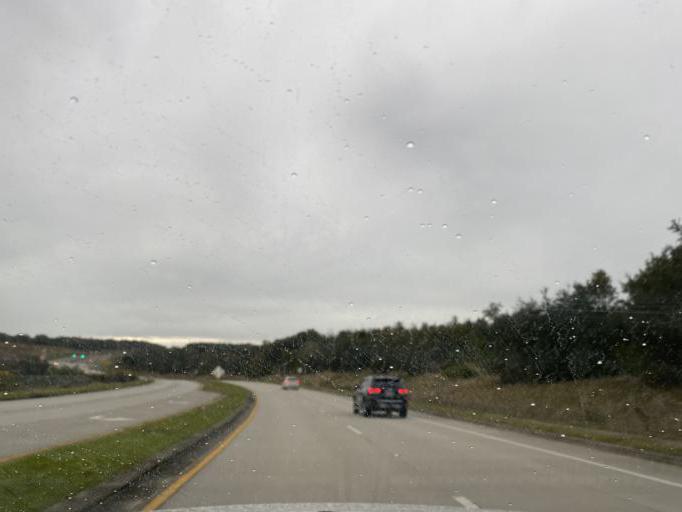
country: US
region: Florida
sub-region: Lake County
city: Minneola
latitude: 28.5446
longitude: -81.7134
